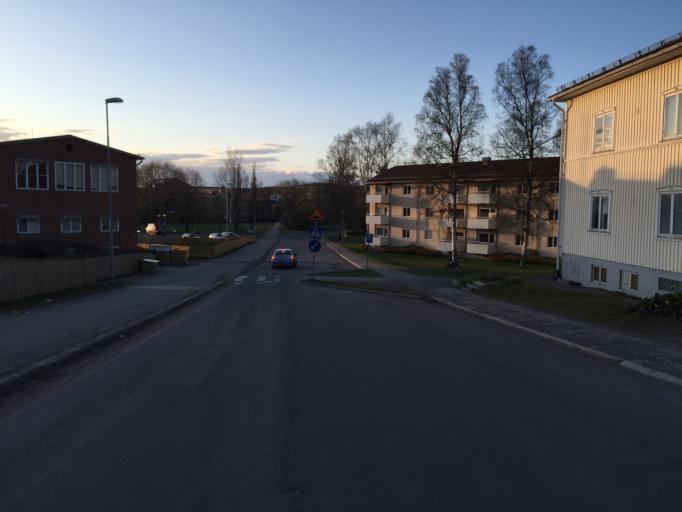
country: SE
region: Dalarna
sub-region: Ludvika Kommun
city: Ludvika
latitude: 60.1445
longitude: 15.1873
